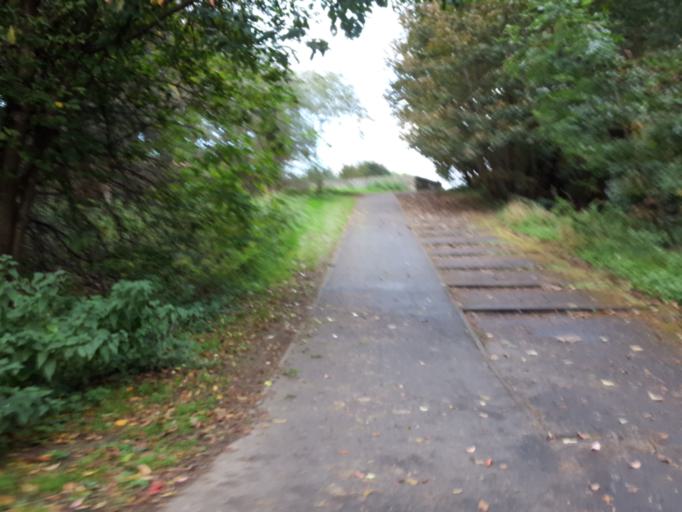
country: GB
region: Scotland
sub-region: West Lothian
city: Livingston
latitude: 55.8891
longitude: -3.5441
